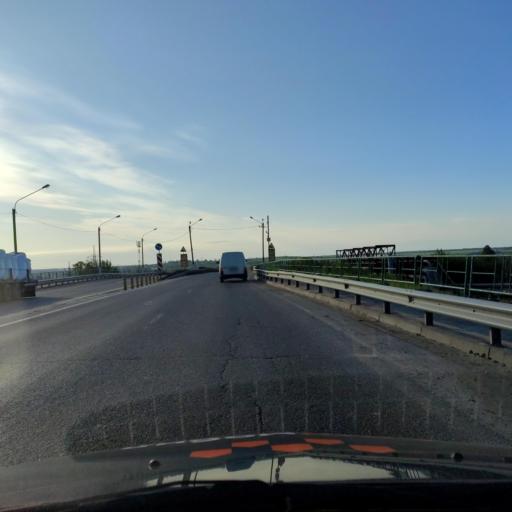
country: RU
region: Lipetsk
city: Yelets
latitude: 52.5920
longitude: 38.4912
